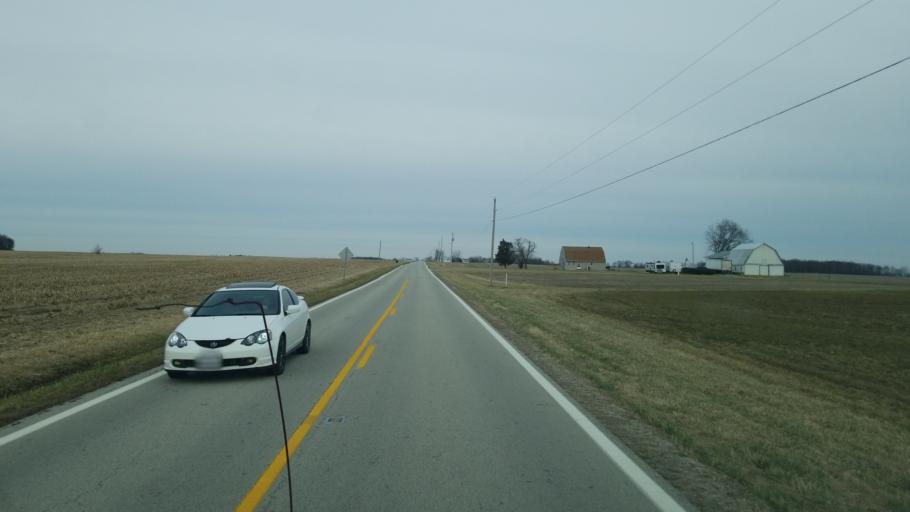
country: US
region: Ohio
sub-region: Ross County
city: Frankfort
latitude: 39.4680
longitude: -83.2020
